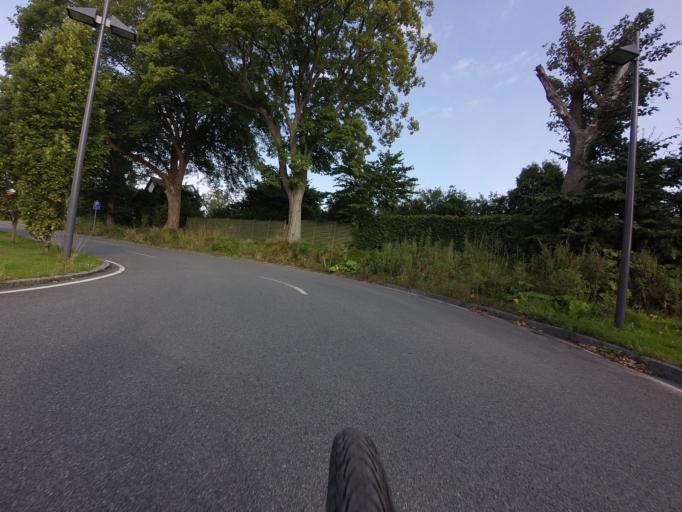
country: DK
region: Zealand
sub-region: Soro Kommune
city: Frederiksberg
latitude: 55.4198
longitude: 11.5699
